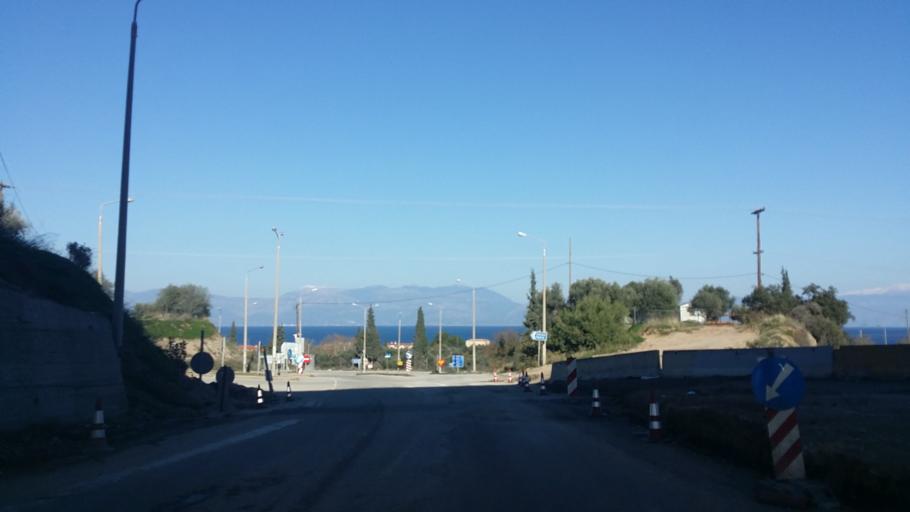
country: GR
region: West Greece
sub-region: Nomos Achaias
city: Akrata
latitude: 38.1760
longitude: 22.2392
